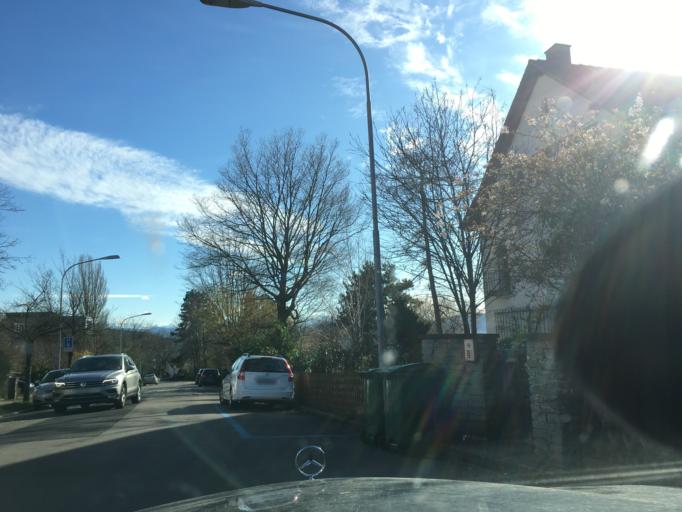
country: CH
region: Zurich
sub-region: Bezirk Zuerich
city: Zuerich (Kreis 7) / Witikon
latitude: 47.3579
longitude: 8.5837
